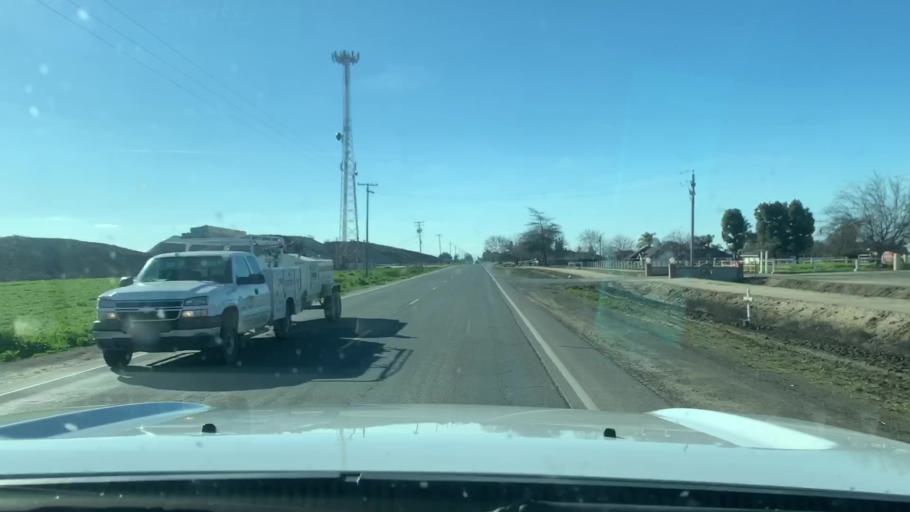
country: US
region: California
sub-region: Kings County
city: Home Garden
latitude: 36.2110
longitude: -119.6068
